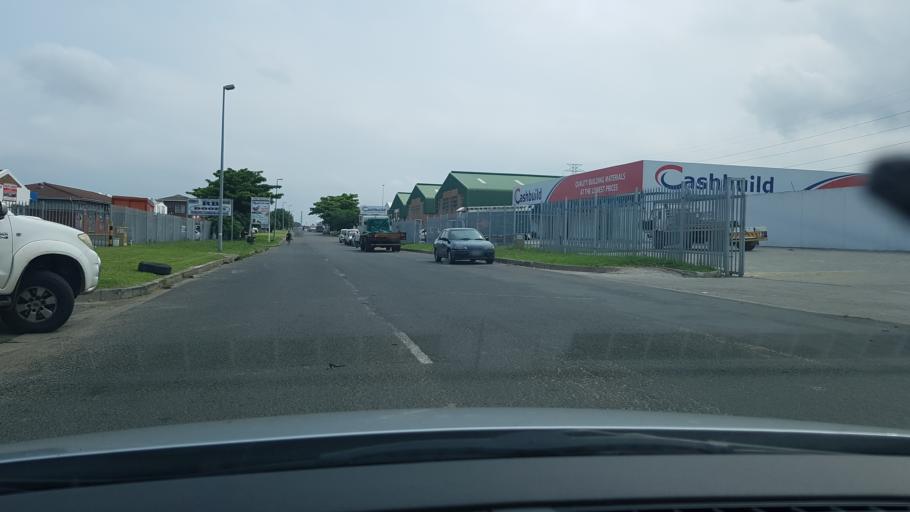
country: ZA
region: KwaZulu-Natal
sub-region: uThungulu District Municipality
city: Richards Bay
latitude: -28.7445
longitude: 32.0488
